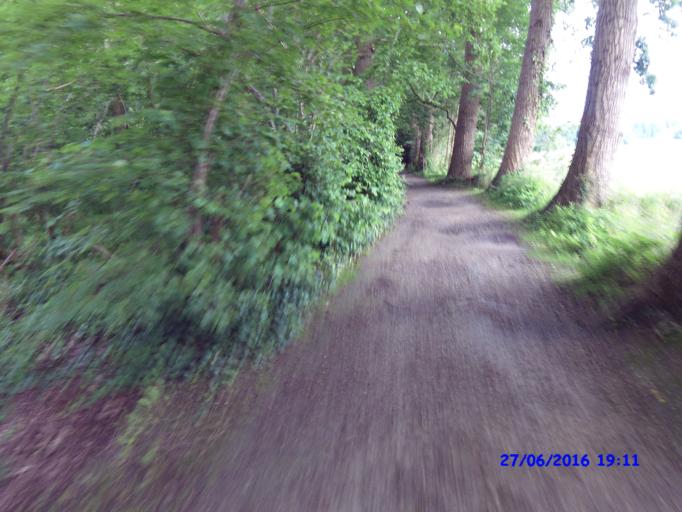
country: BE
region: Flanders
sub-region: Provincie Vlaams-Brabant
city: Wemmel
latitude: 50.8855
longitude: 4.2955
